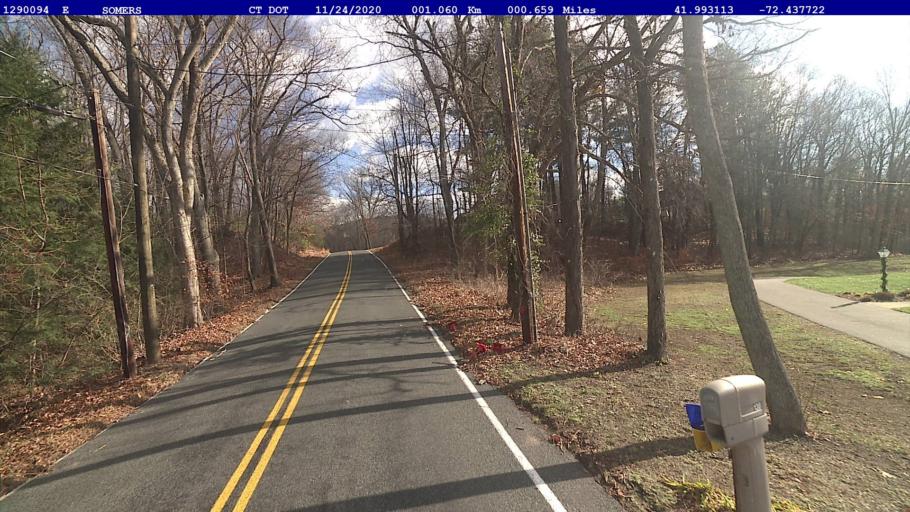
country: US
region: Connecticut
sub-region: Tolland County
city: Somers
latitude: 41.9931
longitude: -72.4377
